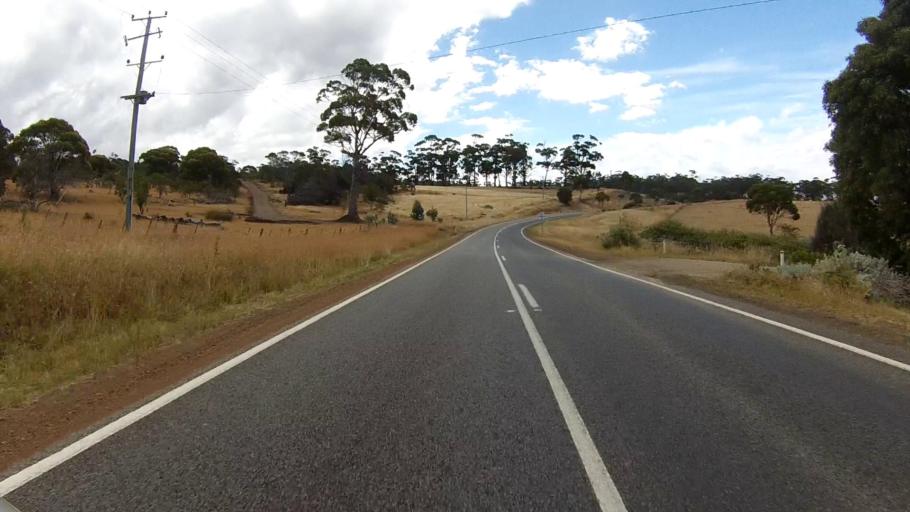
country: AU
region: Tasmania
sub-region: Sorell
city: Sorell
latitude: -42.2159
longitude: 148.0307
